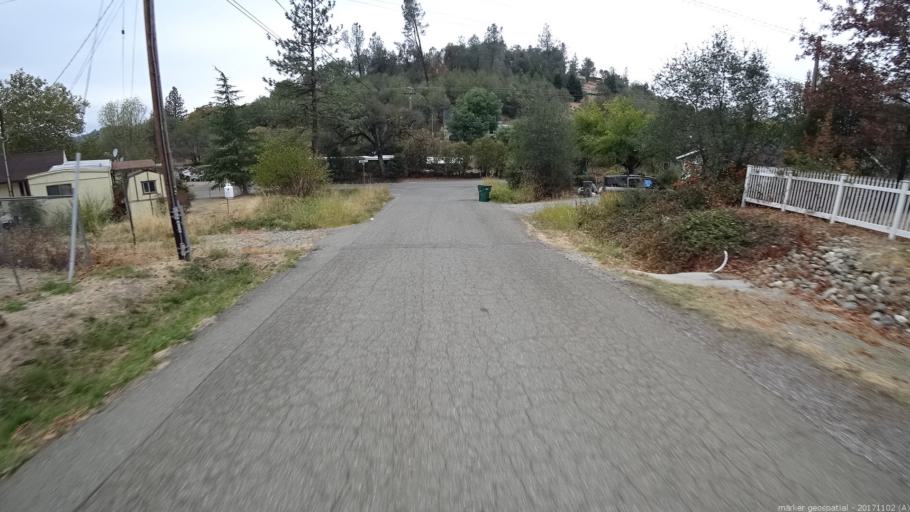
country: US
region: California
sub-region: Shasta County
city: Bella Vista
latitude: 40.7145
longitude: -122.2355
